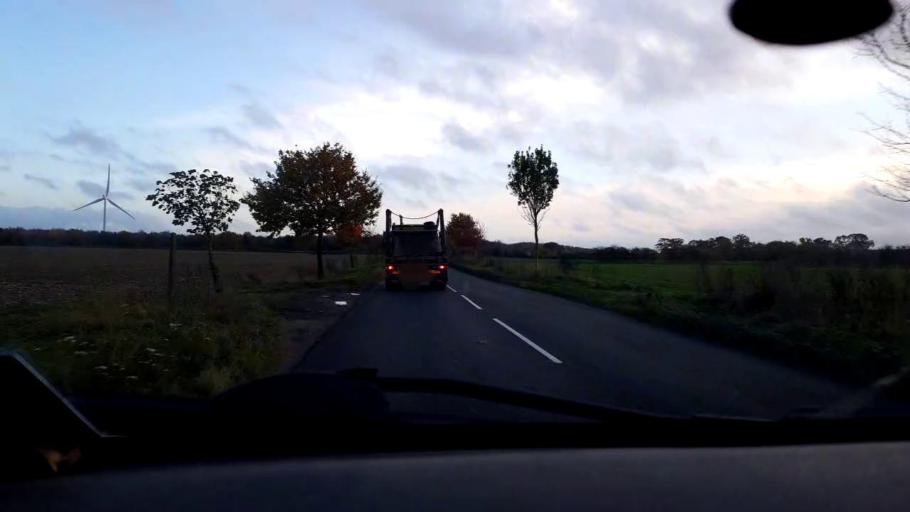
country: GB
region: England
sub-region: Norfolk
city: Mattishall
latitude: 52.7003
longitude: 1.0991
